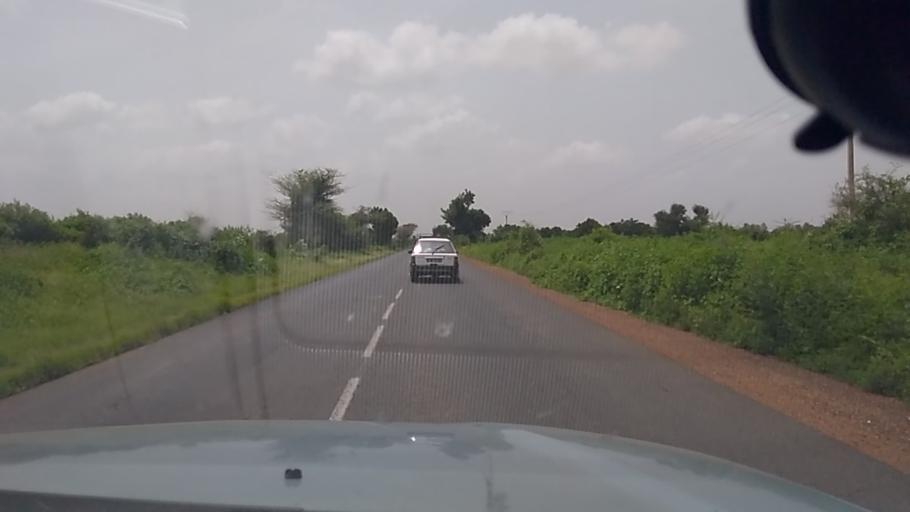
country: SN
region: Thies
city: Mekhe
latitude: 15.0340
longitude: -16.7186
